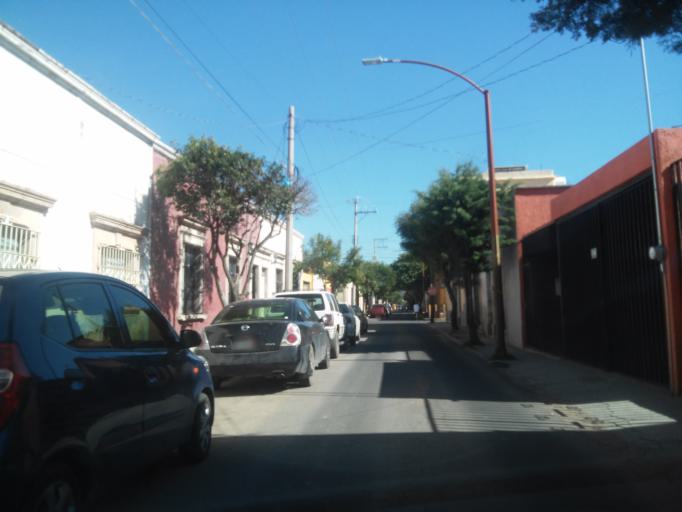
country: MX
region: Durango
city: Victoria de Durango
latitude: 24.0282
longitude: -104.6691
